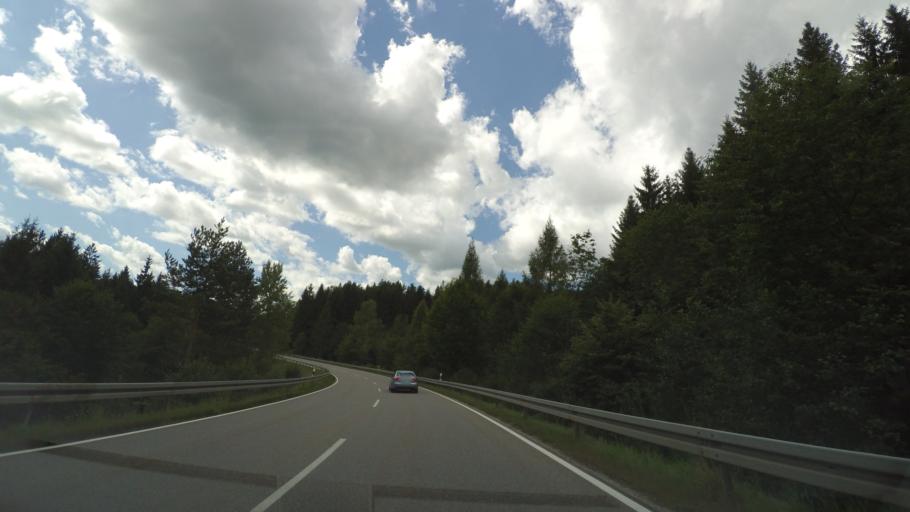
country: DE
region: Bavaria
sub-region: Lower Bavaria
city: Bobrach
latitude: 49.0569
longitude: 13.0488
